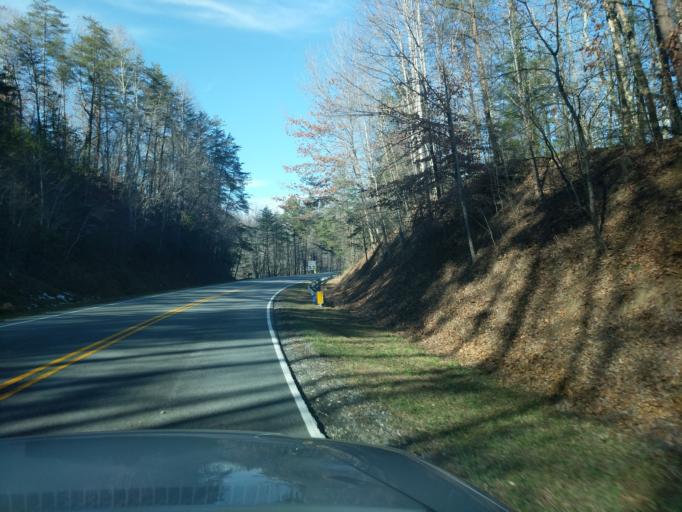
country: US
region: North Carolina
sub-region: McDowell County
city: West Marion
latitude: 35.5541
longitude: -81.9693
